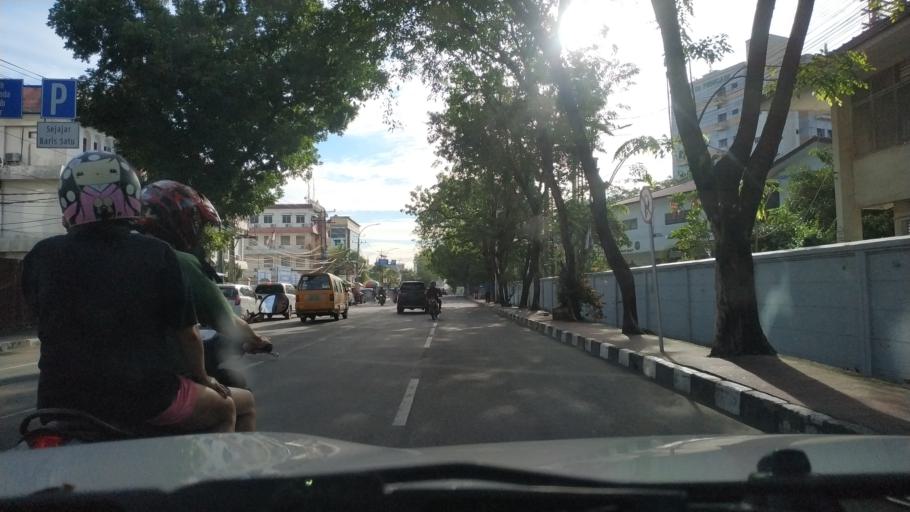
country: ID
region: North Sumatra
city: Medan
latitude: 3.5988
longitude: 98.6872
